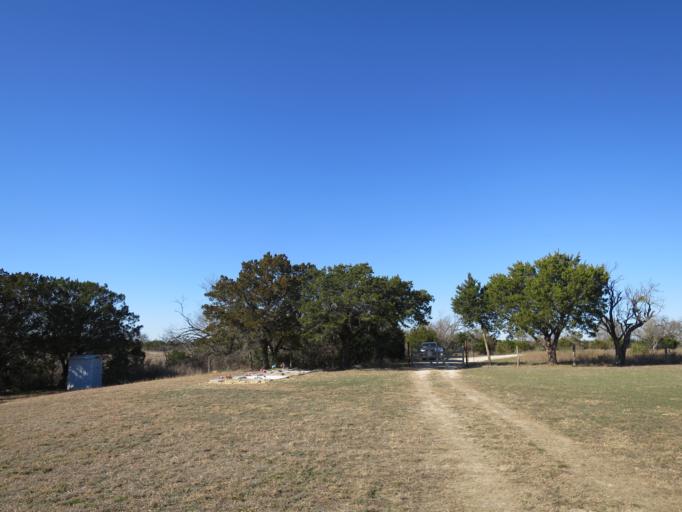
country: US
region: Texas
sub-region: Lampasas County
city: Lampasas
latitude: 30.9412
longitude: -98.1593
